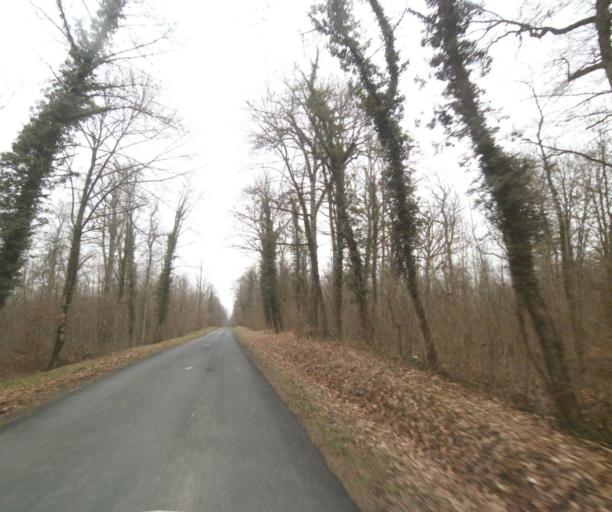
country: FR
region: Champagne-Ardenne
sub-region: Departement de la Haute-Marne
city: Bienville
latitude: 48.5664
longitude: 5.0172
